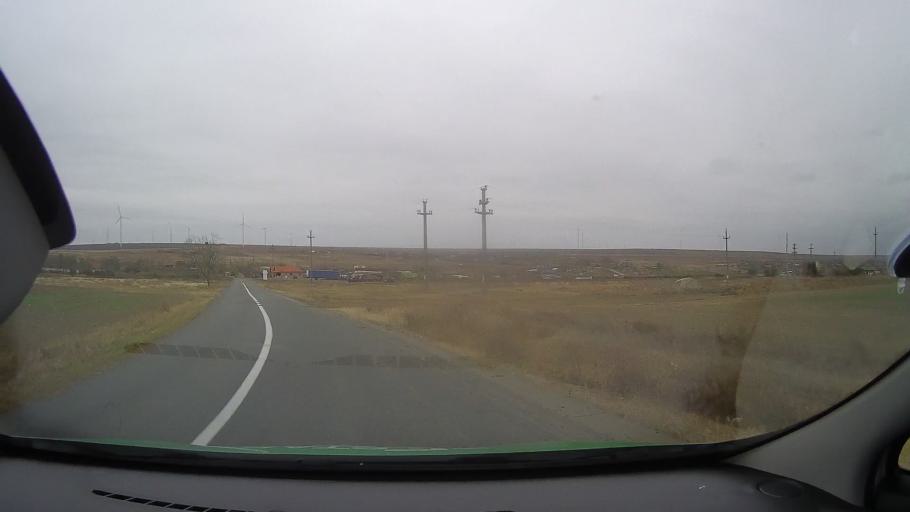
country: RO
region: Constanta
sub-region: Comuna Targusor
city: Targusor
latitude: 44.4889
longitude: 28.3640
